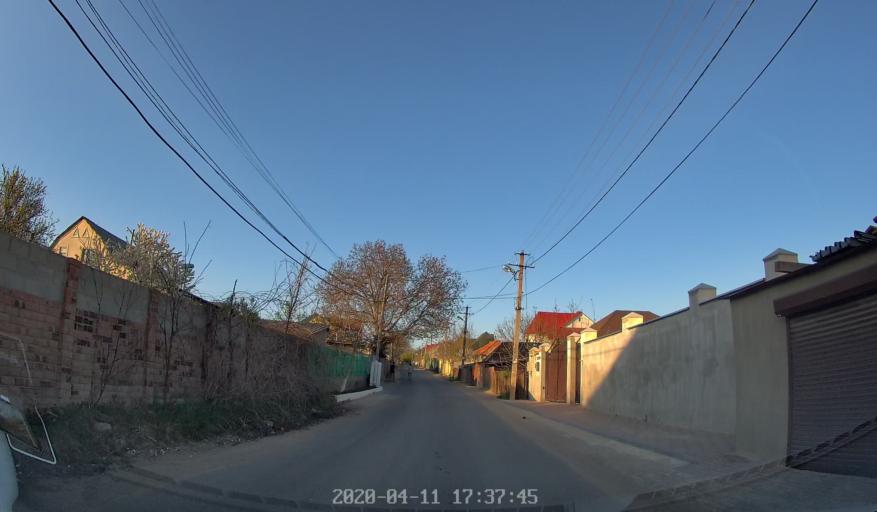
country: MD
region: Laloveni
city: Ialoveni
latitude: 46.9795
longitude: 28.8013
